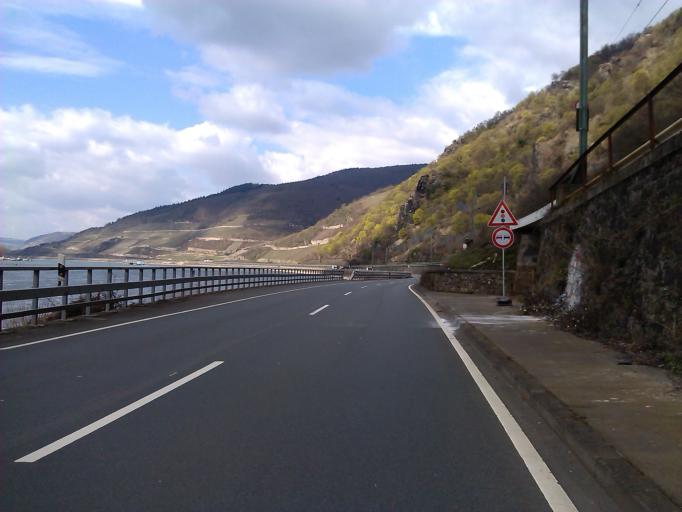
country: DE
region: Rheinland-Pfalz
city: Trechtingshausen
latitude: 50.0056
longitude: 7.8609
